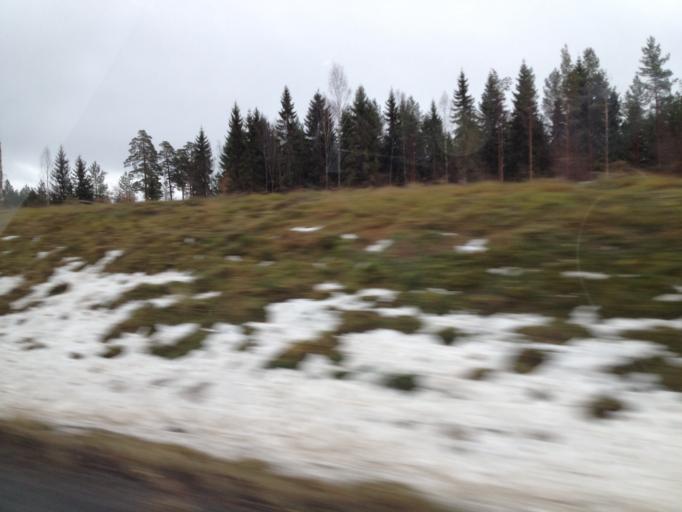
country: FI
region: Uusimaa
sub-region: Raaseporin
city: Ekenaes
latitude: 59.9552
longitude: 23.3639
